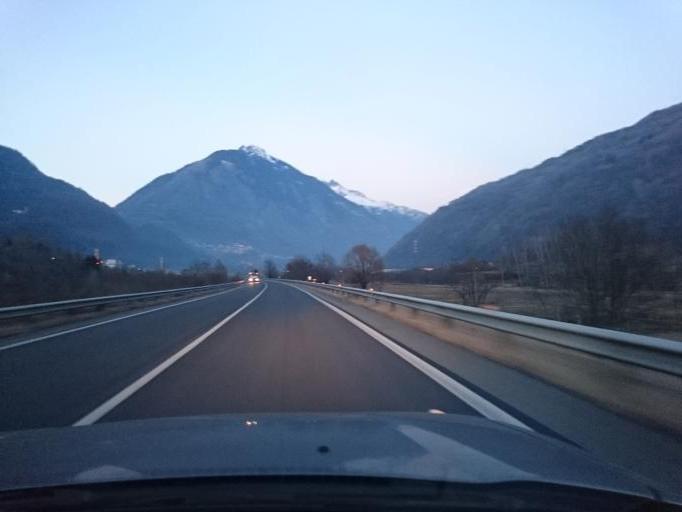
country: IT
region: Lombardy
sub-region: Provincia di Sondrio
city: Mazzo di Valtellina
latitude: 46.2691
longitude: 10.2589
